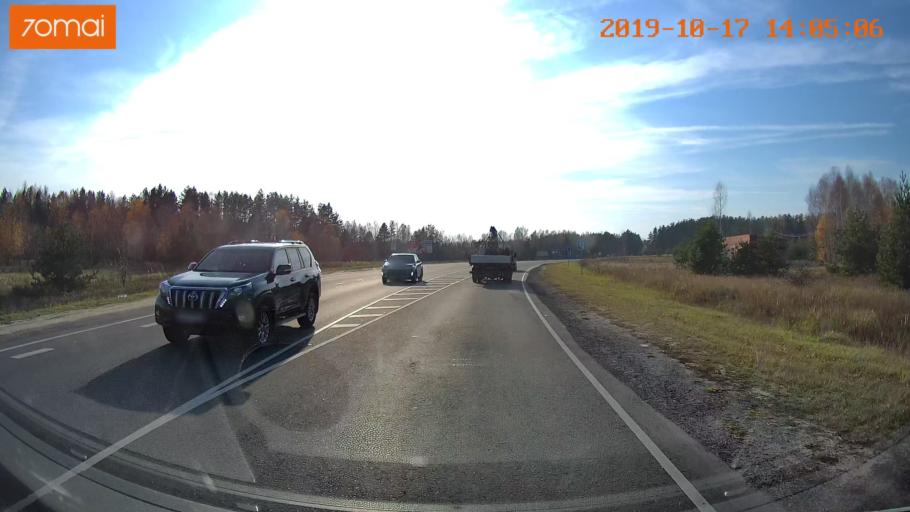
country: RU
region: Rjazan
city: Spas-Klepiki
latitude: 55.1190
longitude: 40.1305
